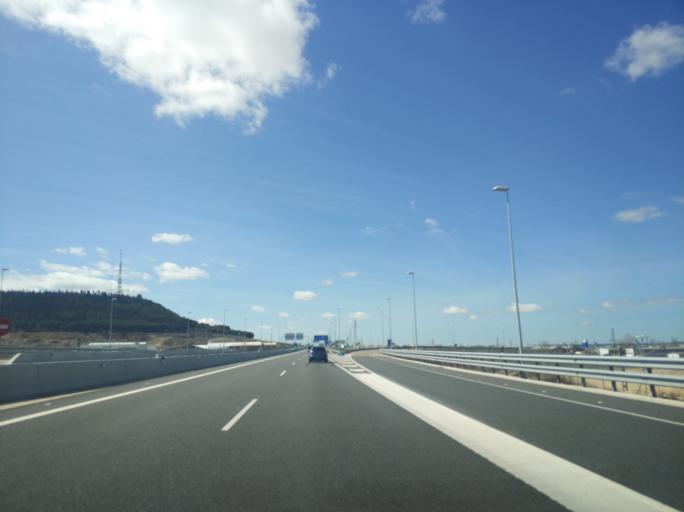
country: ES
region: Castille and Leon
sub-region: Provincia de Valladolid
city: Cisterniga
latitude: 41.6231
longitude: -4.6900
